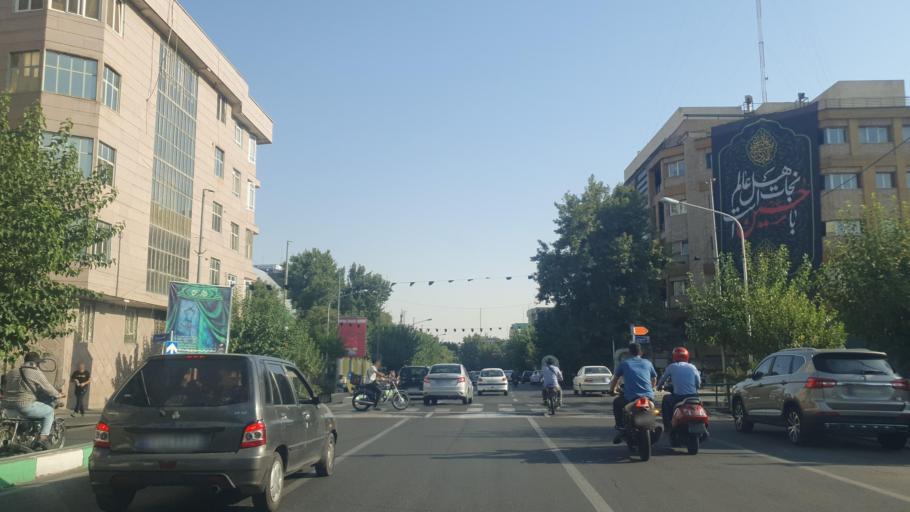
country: IR
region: Tehran
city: Tehran
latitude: 35.7128
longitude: 51.4257
